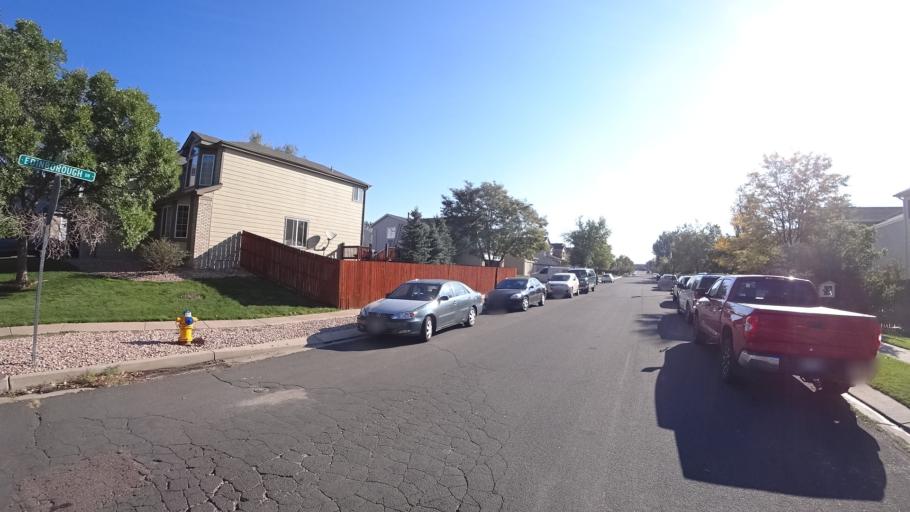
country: US
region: Colorado
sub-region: El Paso County
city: Cimarron Hills
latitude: 38.8804
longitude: -104.6983
